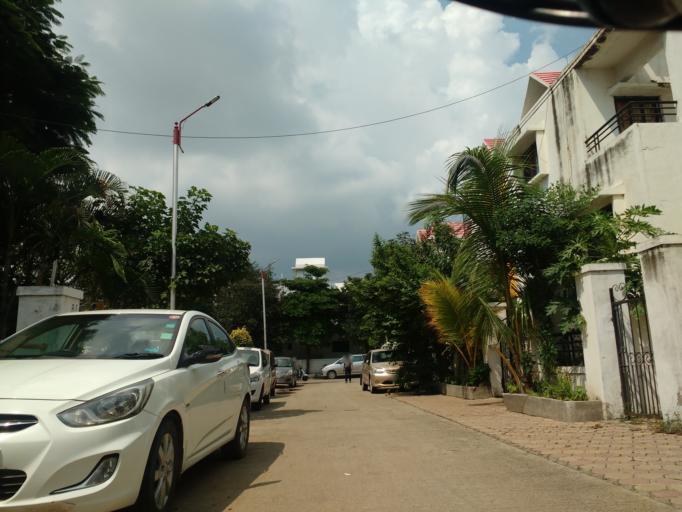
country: IN
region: Maharashtra
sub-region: Aurangabad Division
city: Aurangabad
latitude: 19.8588
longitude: 75.3039
